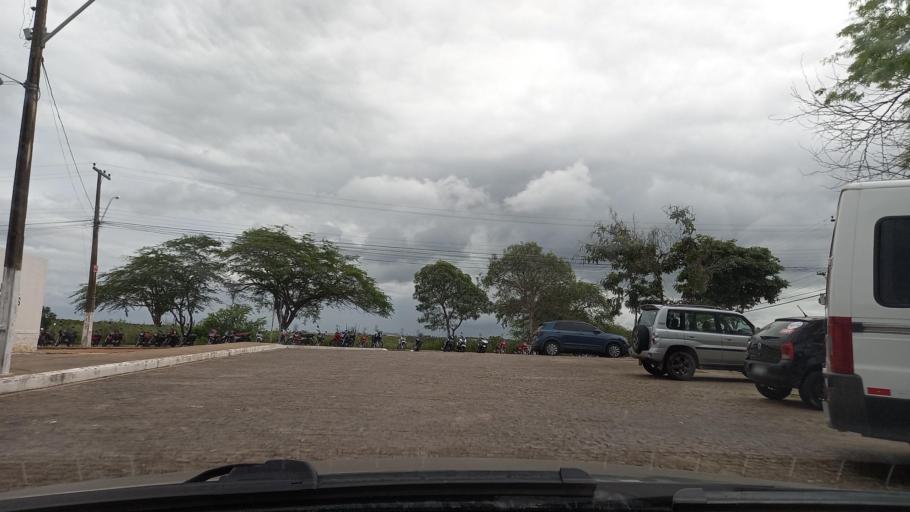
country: BR
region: Sergipe
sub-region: Caninde De Sao Francisco
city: Caninde de Sao Francisco
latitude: -9.6218
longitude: -37.7657
